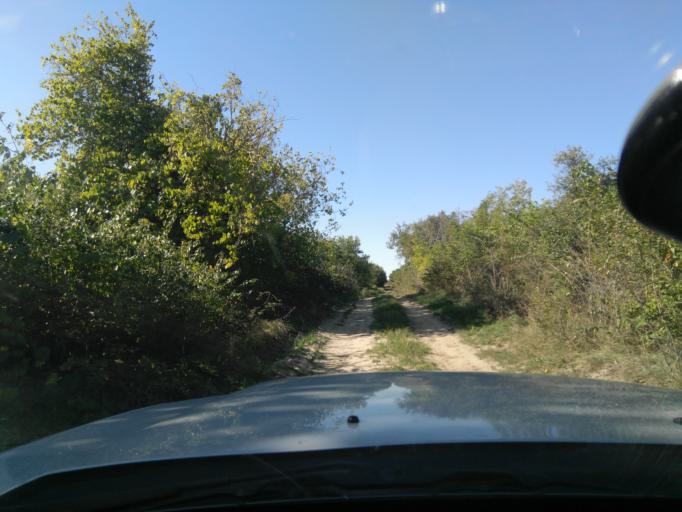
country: HU
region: Fejer
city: Pazmand
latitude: 47.3048
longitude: 18.7034
